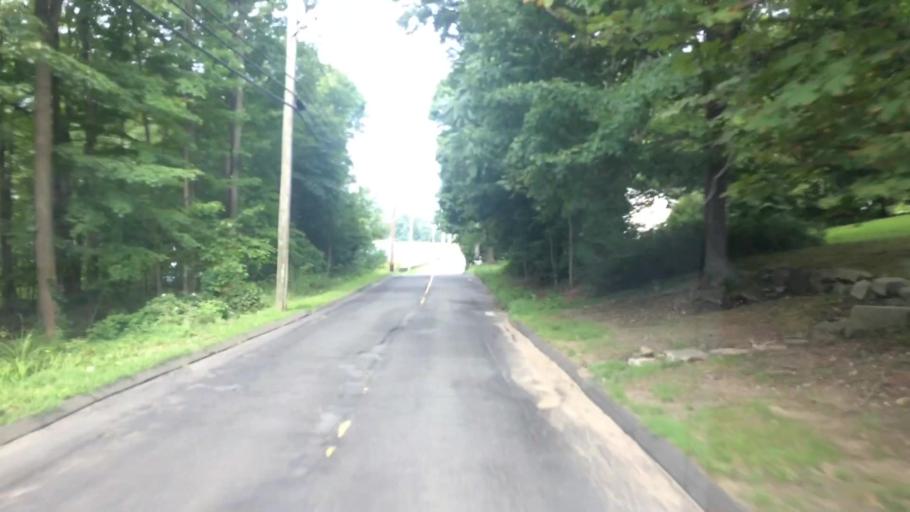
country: US
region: Connecticut
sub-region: Fairfield County
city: Danbury
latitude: 41.4098
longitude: -73.5026
